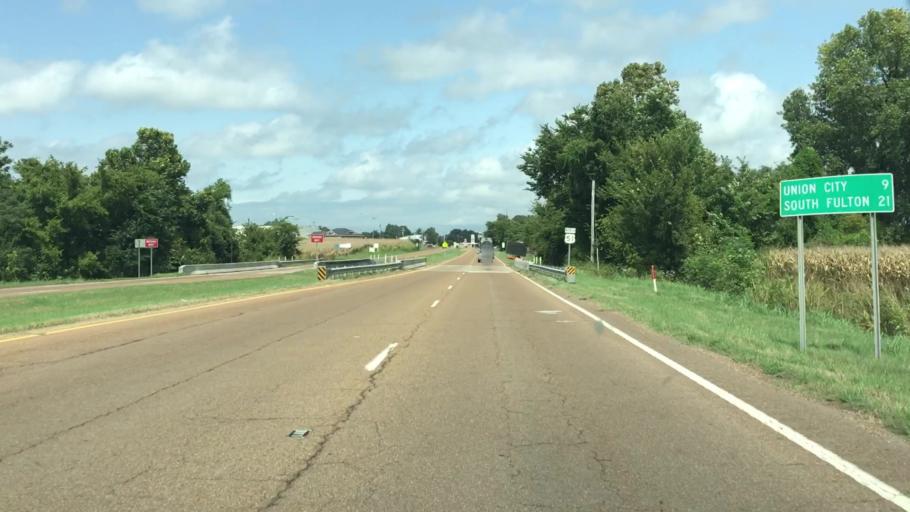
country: US
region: Tennessee
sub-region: Obion County
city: Troy
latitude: 36.3386
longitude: -89.1566
